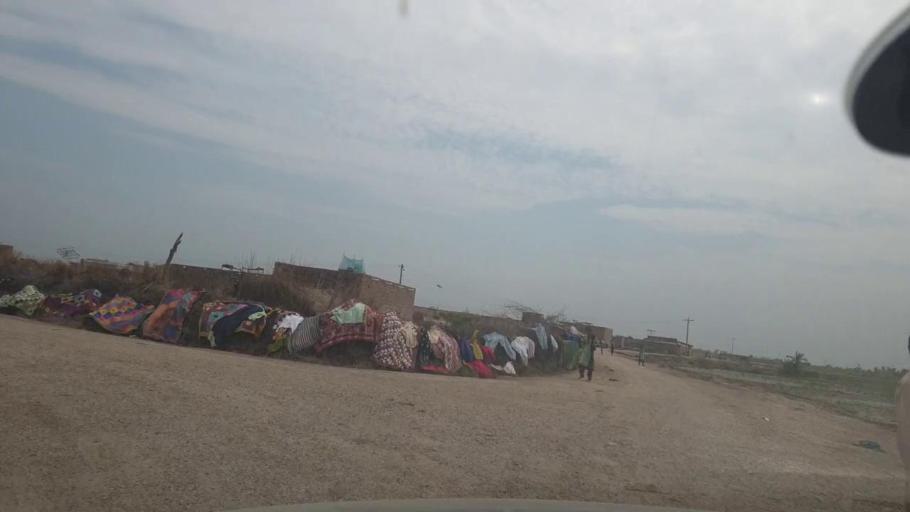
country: PK
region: Balochistan
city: Mehrabpur
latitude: 28.0518
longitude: 68.1364
